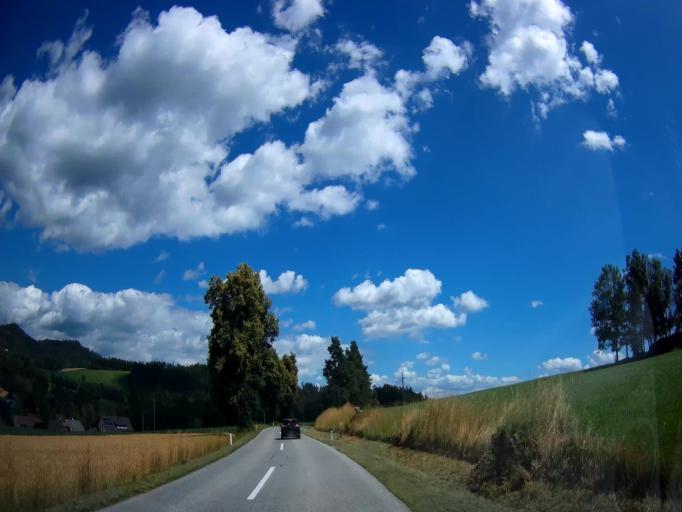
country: AT
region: Carinthia
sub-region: Politischer Bezirk Sankt Veit an der Glan
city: St. Georgen am Laengsee
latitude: 46.7154
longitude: 14.4166
